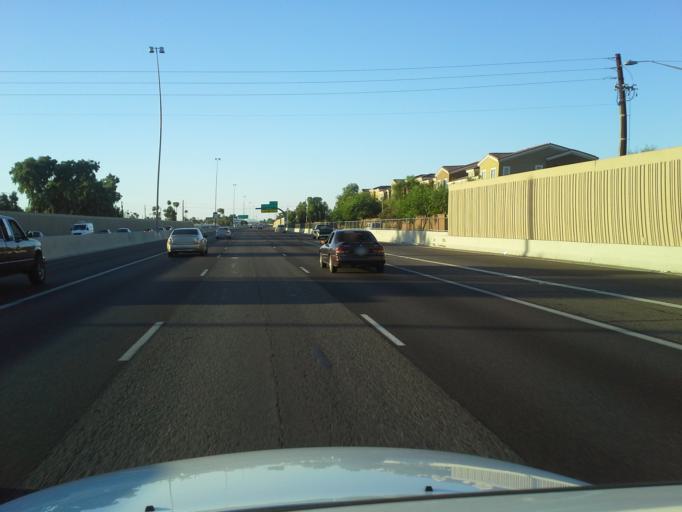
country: US
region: Arizona
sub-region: Maricopa County
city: Phoenix
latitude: 33.4983
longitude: -112.1128
